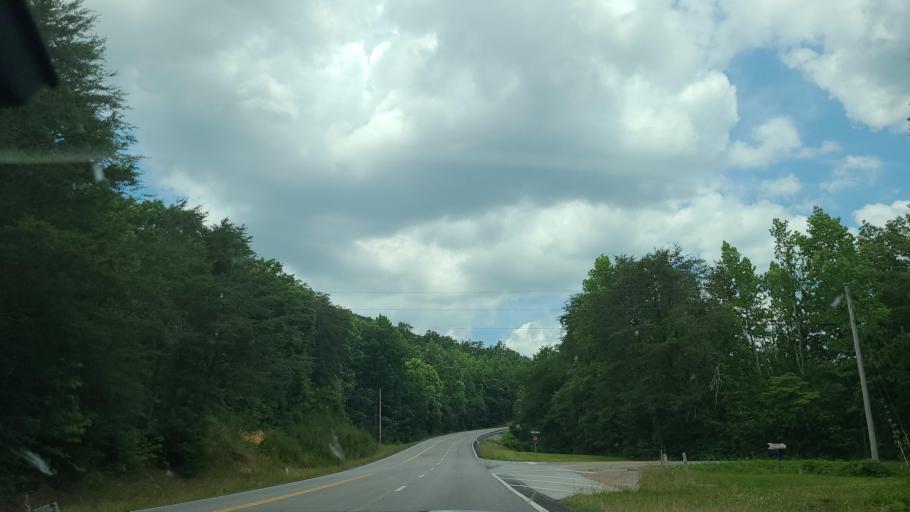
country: US
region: Tennessee
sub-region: Cumberland County
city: Lake Tansi
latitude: 35.7559
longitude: -85.0562
